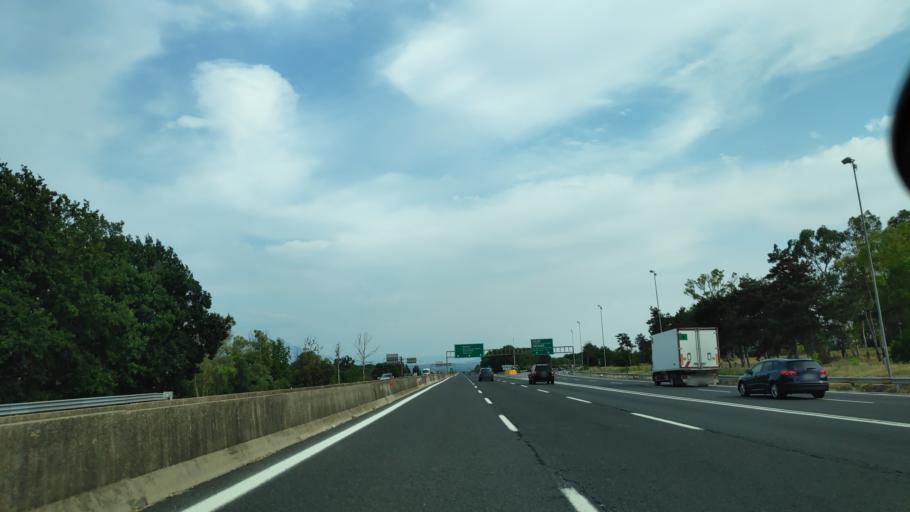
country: IT
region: Latium
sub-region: Citta metropolitana di Roma Capitale
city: Fiano Romano
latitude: 42.1683
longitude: 12.6131
